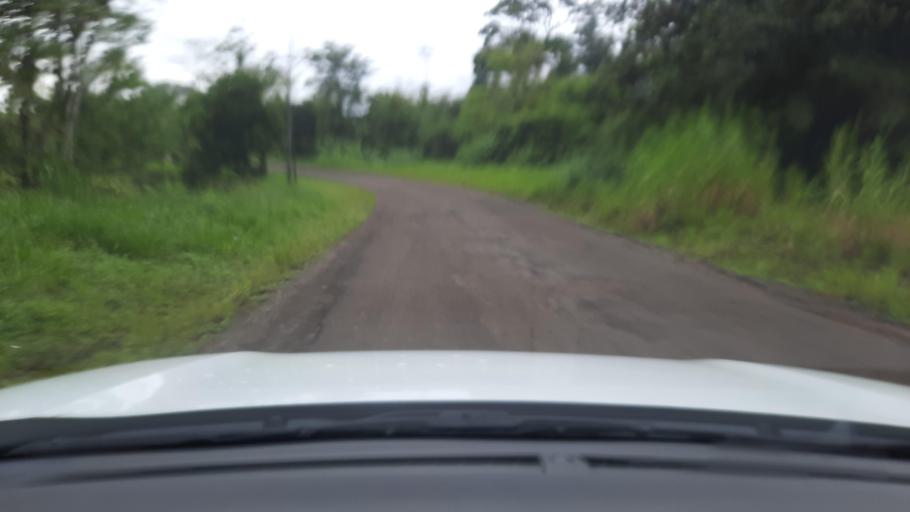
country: CR
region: Alajuela
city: San Jose
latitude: 11.0041
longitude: -85.3168
